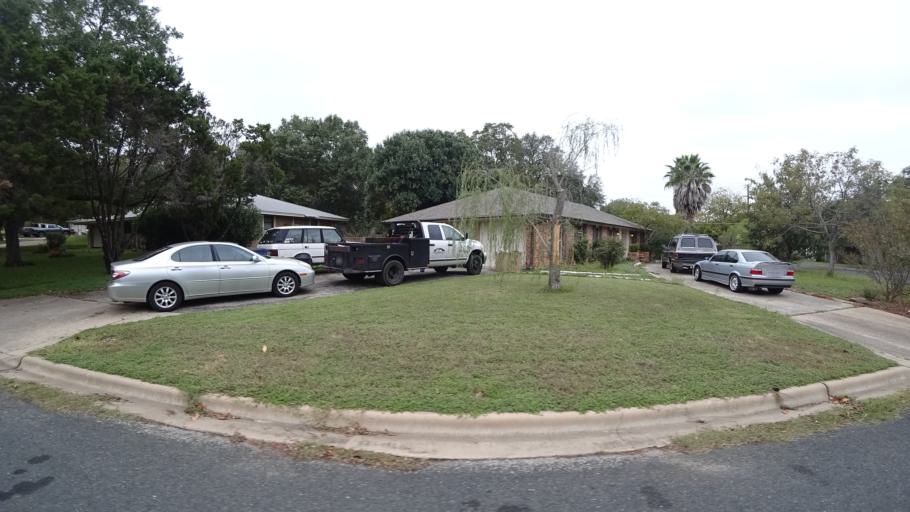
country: US
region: Texas
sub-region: Travis County
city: Barton Creek
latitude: 30.2360
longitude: -97.8802
